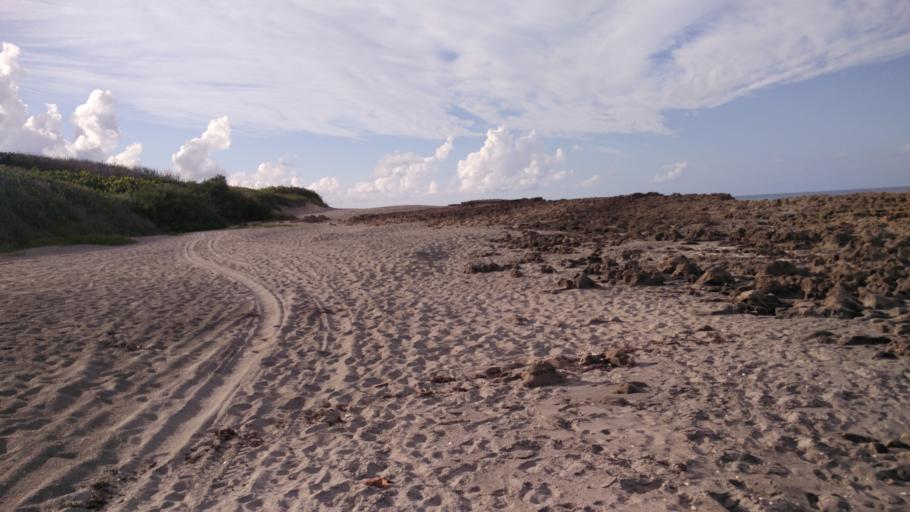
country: US
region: Florida
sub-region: Palm Beach County
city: Jupiter
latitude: 26.9738
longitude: -80.0810
